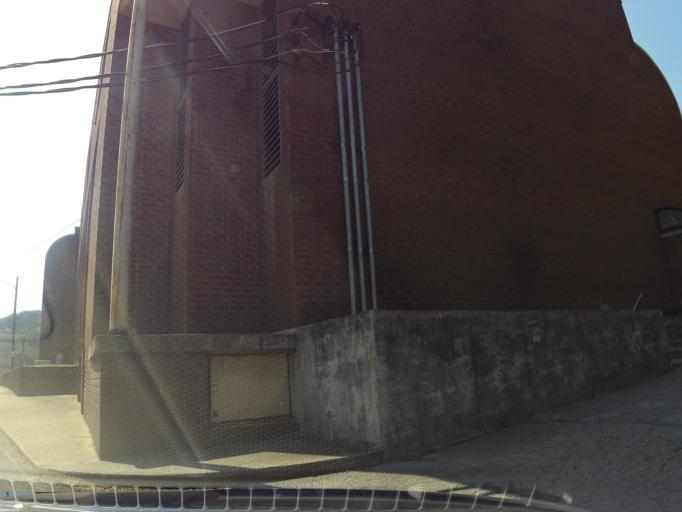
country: US
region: Kentucky
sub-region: Harlan County
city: Harlan
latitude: 36.8473
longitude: -83.3167
